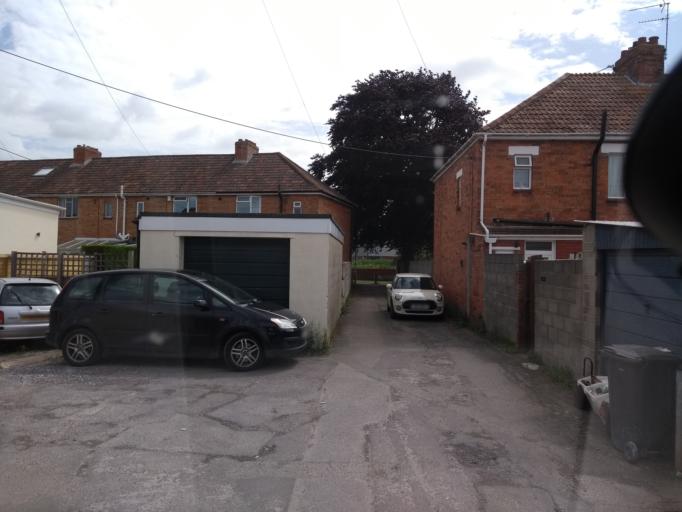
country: GB
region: England
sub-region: Somerset
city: Bridgwater
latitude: 51.1345
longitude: -3.0040
